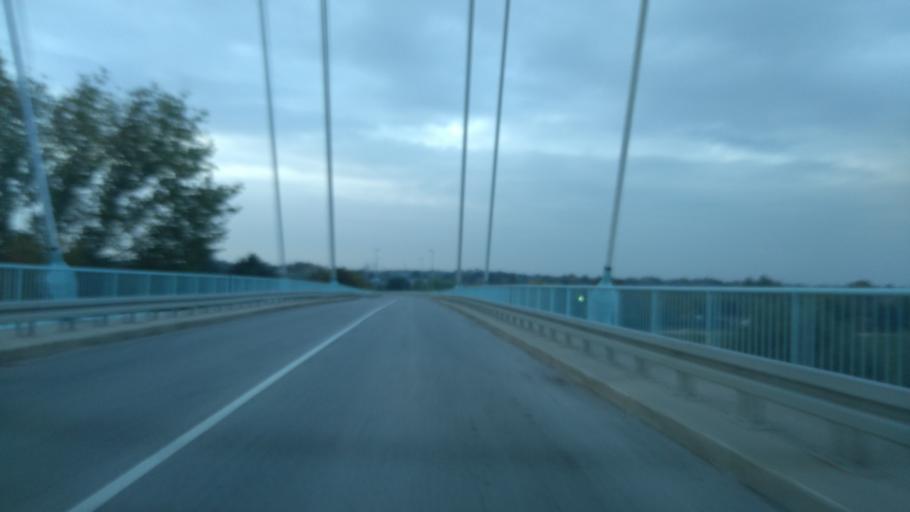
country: RS
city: Mol
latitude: 45.7853
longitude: 20.1455
